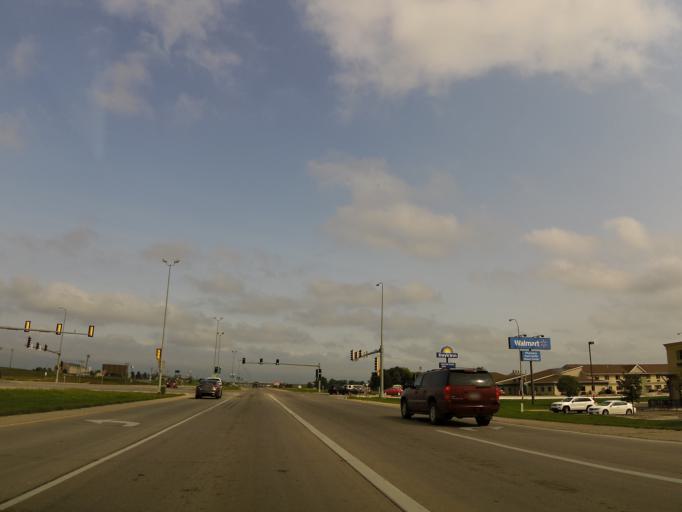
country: US
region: South Dakota
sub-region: Codington County
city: Watertown
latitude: 44.8900
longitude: -97.0692
